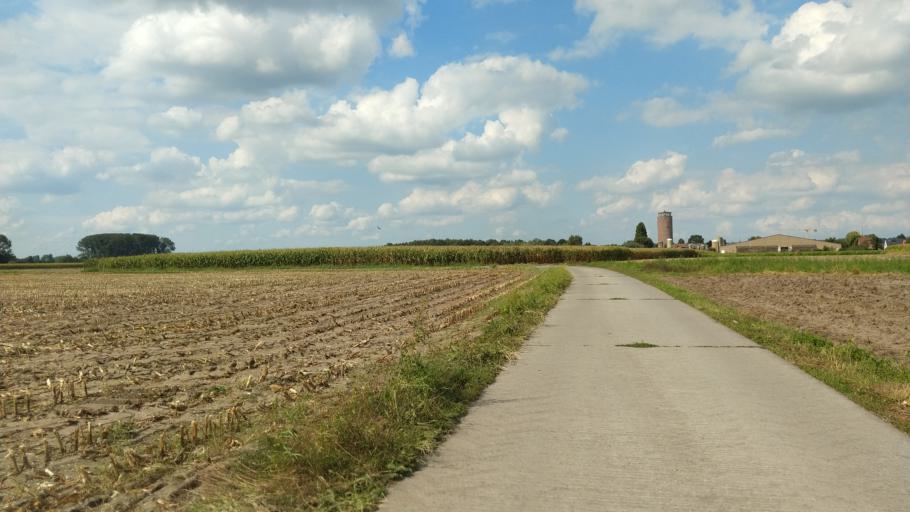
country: BE
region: Flanders
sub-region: Provincie Oost-Vlaanderen
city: Evergem
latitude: 51.1150
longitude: 3.6786
